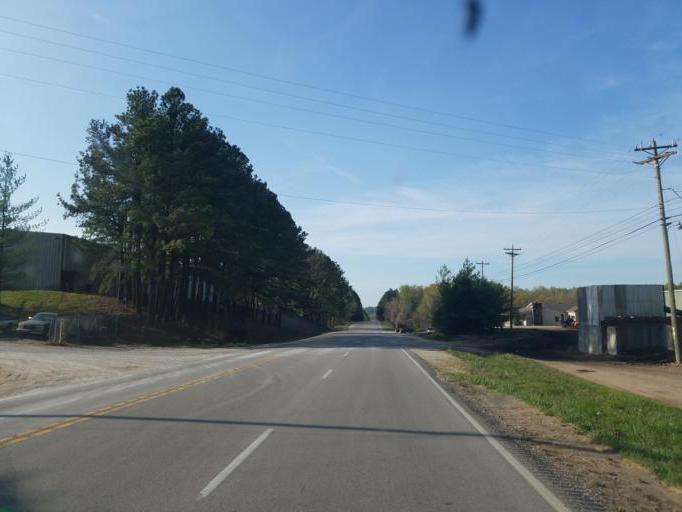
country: US
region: Kentucky
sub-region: Hart County
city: Munfordville
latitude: 37.3215
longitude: -85.9095
